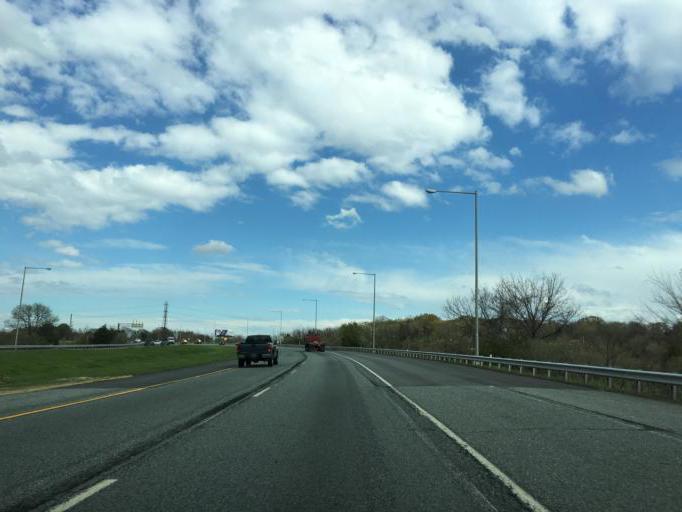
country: US
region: Maryland
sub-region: Baltimore County
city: Dundalk
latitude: 39.2039
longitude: -76.5547
